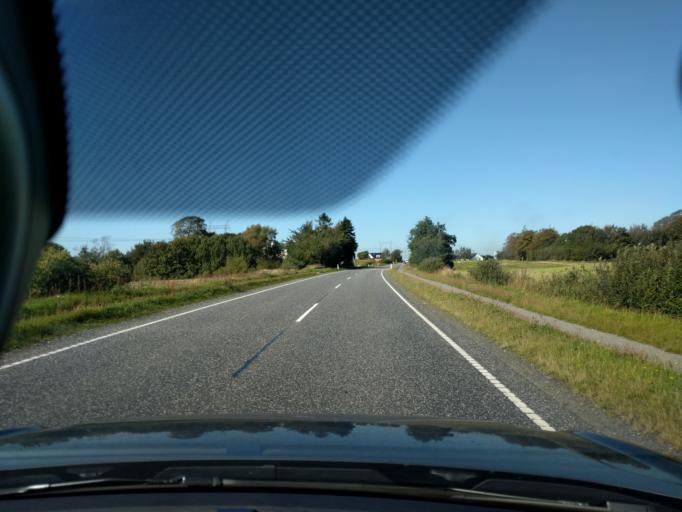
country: DK
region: North Denmark
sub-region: Vesthimmerland Kommune
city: Alestrup
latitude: 56.7168
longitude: 9.6130
